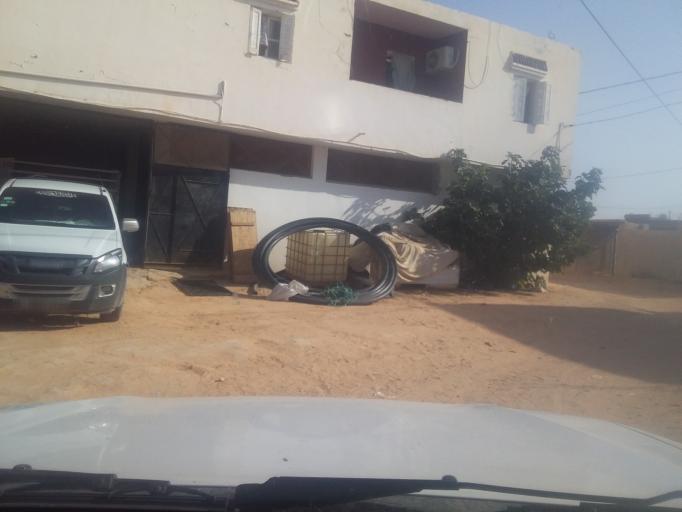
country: TN
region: Qabis
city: Matmata
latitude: 33.6090
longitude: 10.2795
